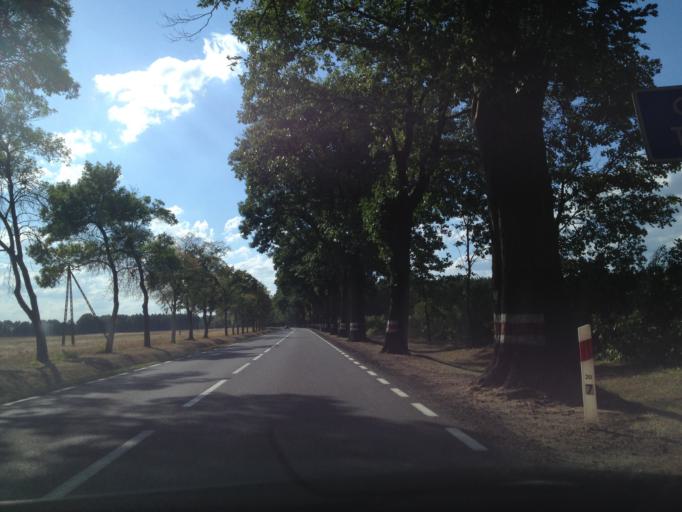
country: PL
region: Lubusz
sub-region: Powiat zarski
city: Lipinki Luzyckie
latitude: 51.6367
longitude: 14.9193
